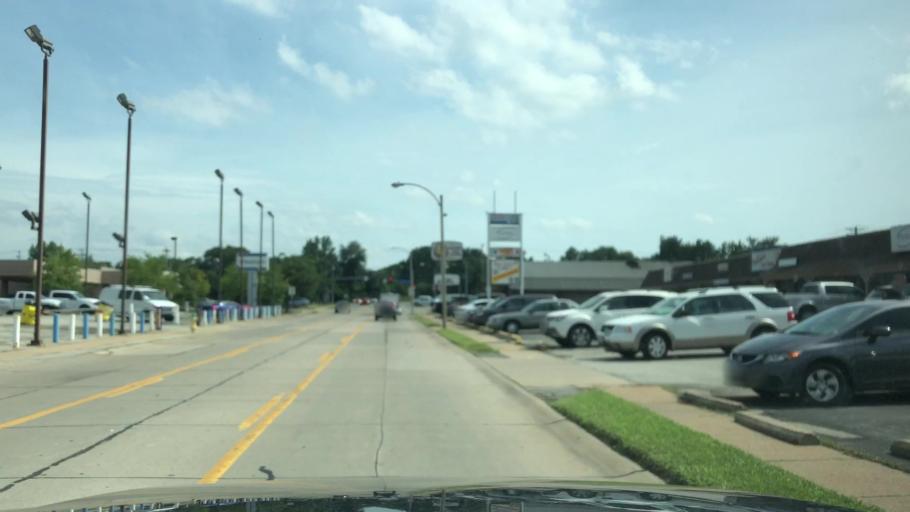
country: US
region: Missouri
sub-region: Saint Charles County
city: Saint Charles
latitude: 38.7861
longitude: -90.5156
